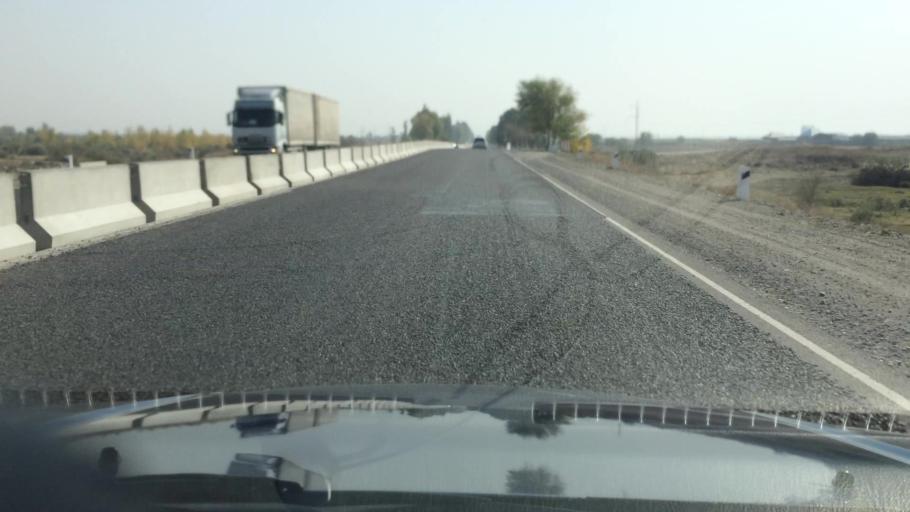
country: KG
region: Chuy
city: Kant
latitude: 42.9705
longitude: 74.9026
